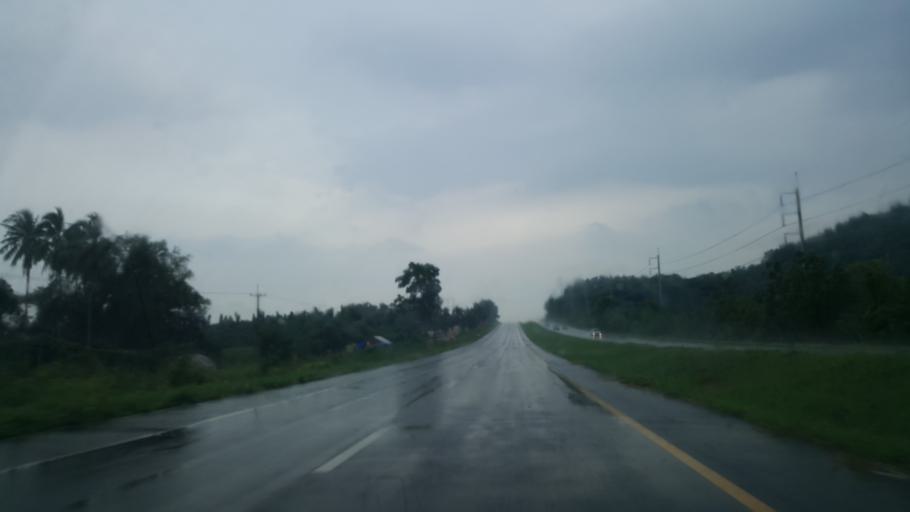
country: TH
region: Chon Buri
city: Ban Talat Bueng
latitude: 12.9904
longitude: 101.0612
